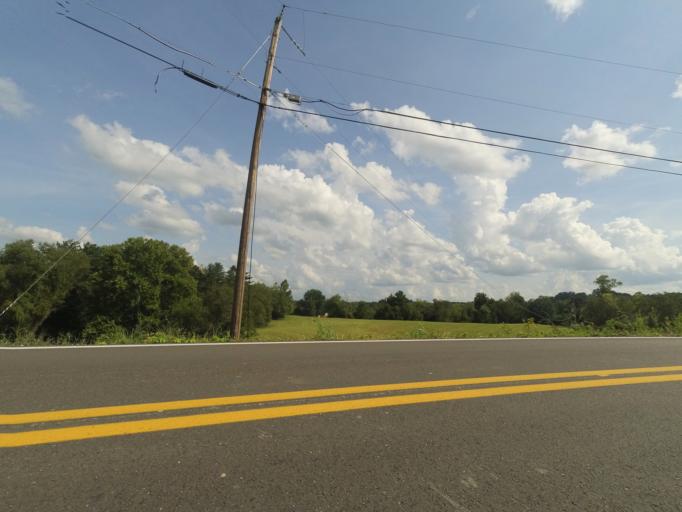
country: US
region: Ohio
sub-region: Lawrence County
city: Burlington
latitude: 38.3742
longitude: -82.5336
